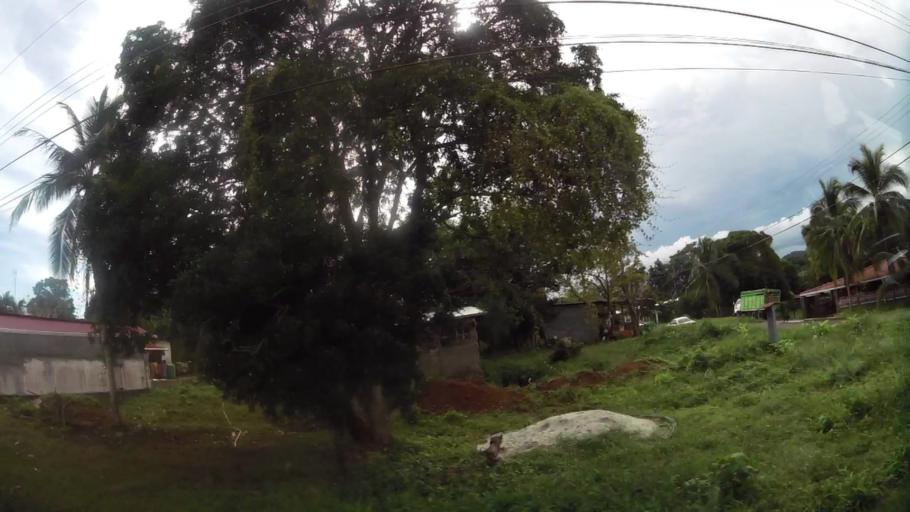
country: PA
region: Panama
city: El Coco
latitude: 8.8709
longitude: -79.8043
